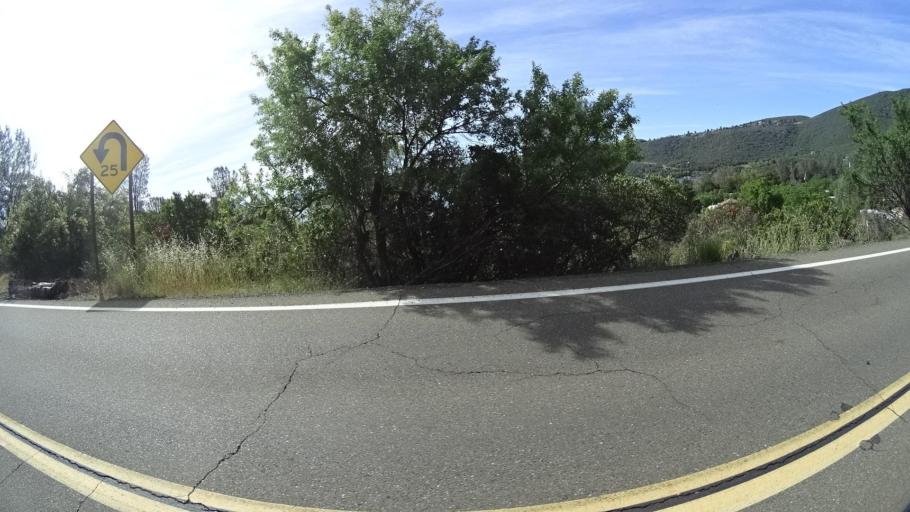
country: US
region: California
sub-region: Lake County
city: Soda Bay
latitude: 38.9822
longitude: -122.7411
